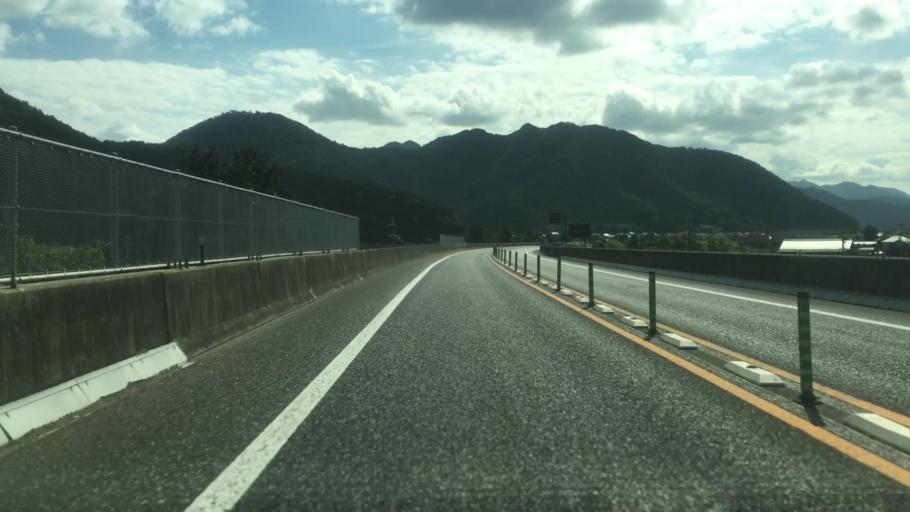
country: JP
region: Kyoto
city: Fukuchiyama
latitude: 35.2265
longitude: 135.0301
